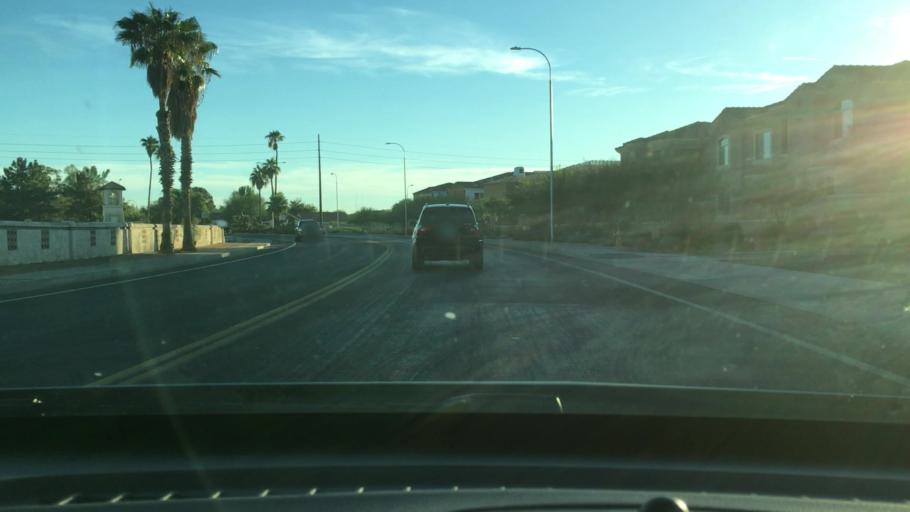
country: US
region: Arizona
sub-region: Maricopa County
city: Chandler
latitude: 33.2933
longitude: -111.8145
